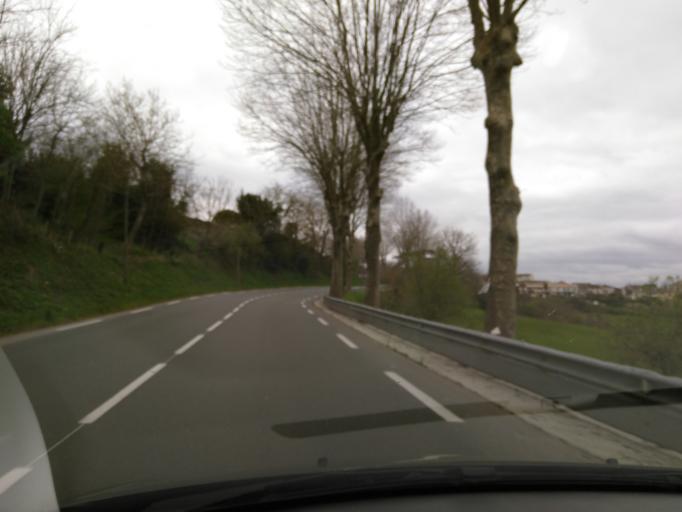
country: FR
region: Aquitaine
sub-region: Departement du Lot-et-Garonne
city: Cancon
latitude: 44.4939
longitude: 0.6695
